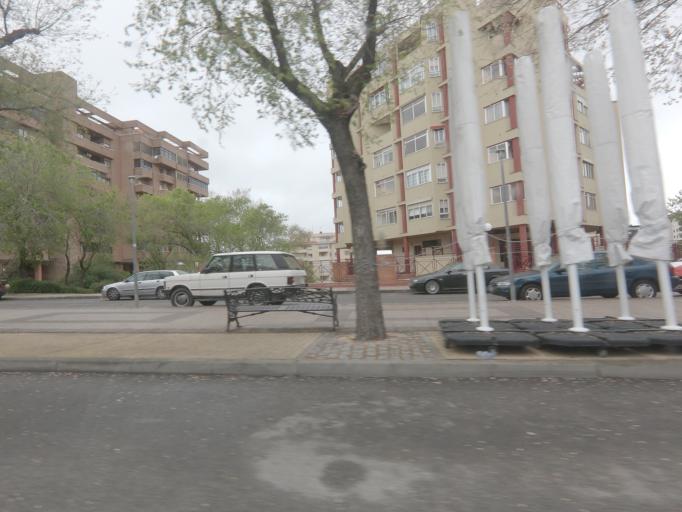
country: ES
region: Extremadura
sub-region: Provincia de Caceres
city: Caceres
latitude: 39.4700
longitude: -6.3846
